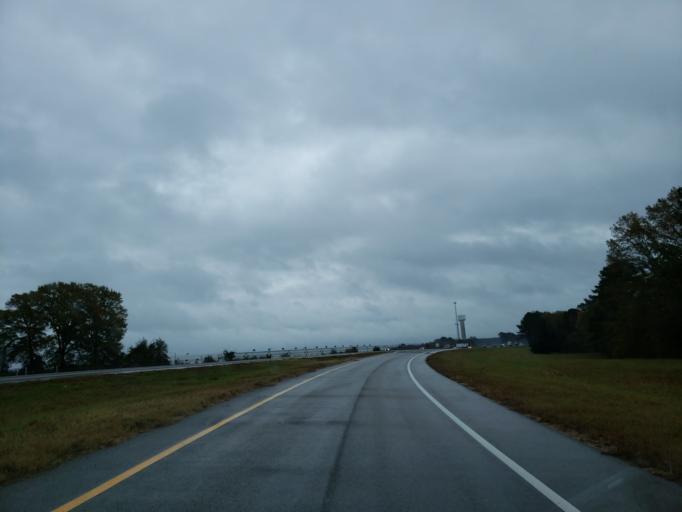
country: US
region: Mississippi
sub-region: Lauderdale County
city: Marion
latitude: 32.3836
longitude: -88.6329
